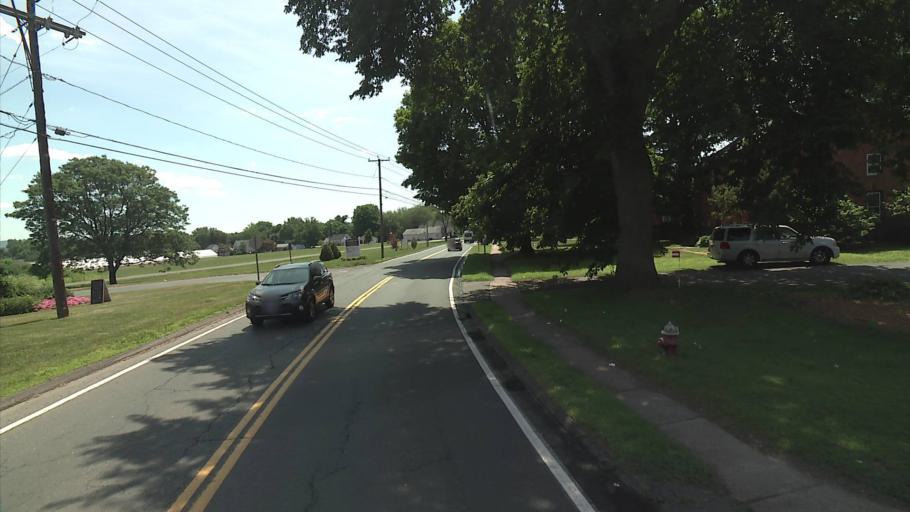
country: US
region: Connecticut
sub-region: Middlesex County
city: Cromwell
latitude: 41.6019
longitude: -72.6566
